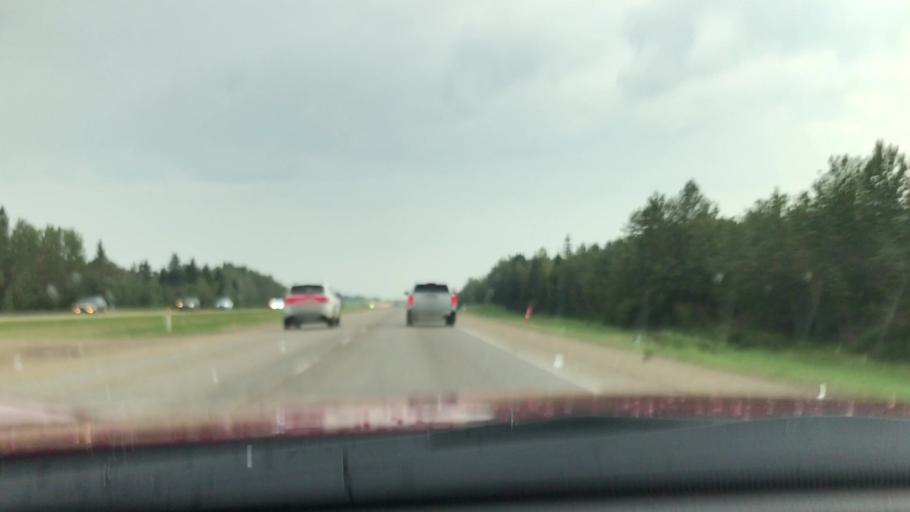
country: CA
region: Alberta
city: Lacombe
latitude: 52.5701
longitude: -113.6624
